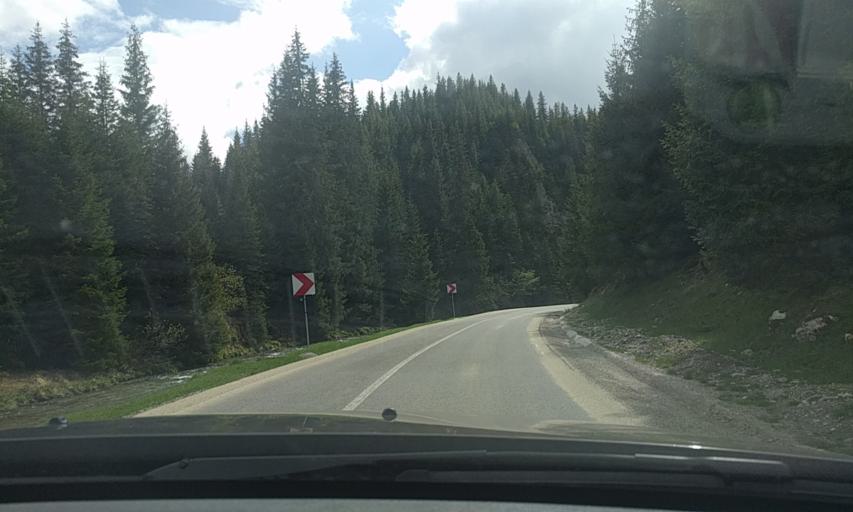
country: RO
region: Prahova
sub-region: Oras Busteni
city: Busteni
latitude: 45.3738
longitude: 25.4357
